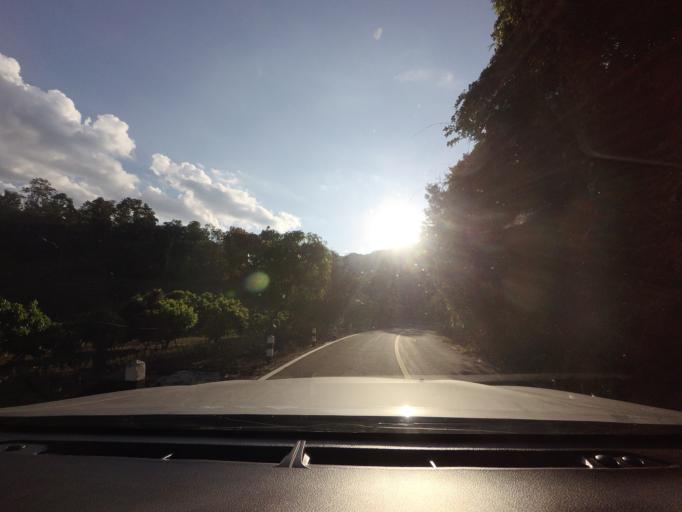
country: TH
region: Chiang Mai
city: Chai Prakan
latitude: 19.5543
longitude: 99.1653
